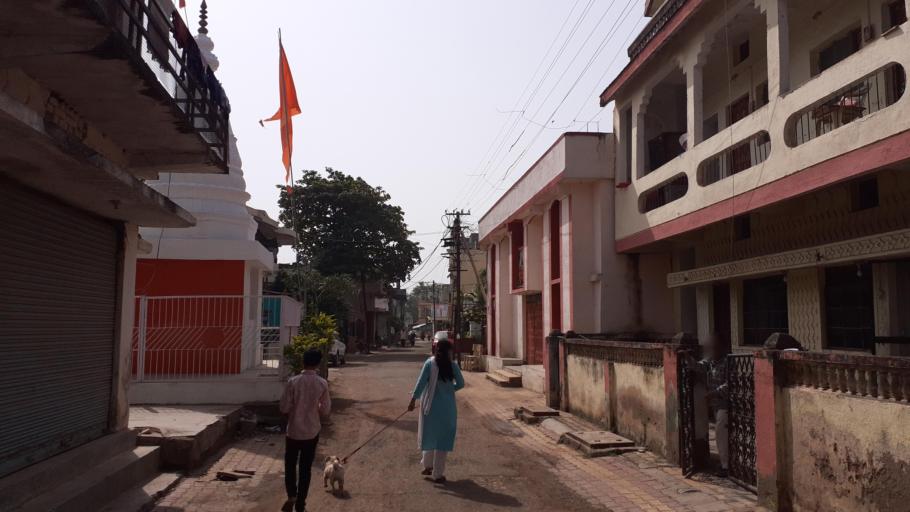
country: IN
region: Maharashtra
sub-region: Chandrapur
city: Ghugus
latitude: 20.1061
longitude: 79.1116
